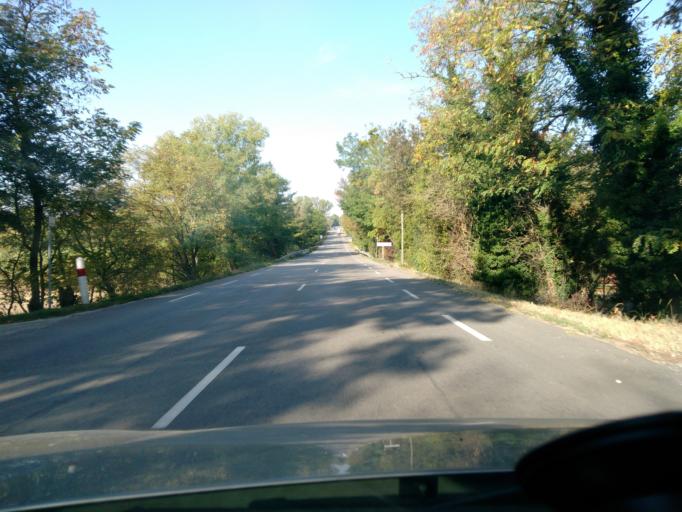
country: FR
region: Rhone-Alpes
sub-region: Departement de la Drome
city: La Garde-Adhemar
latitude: 44.4199
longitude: 4.7853
